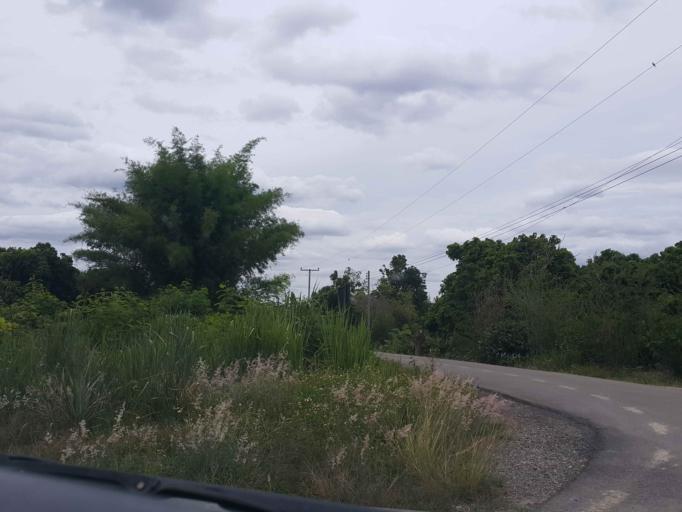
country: TH
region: Chiang Mai
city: Doi Lo
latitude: 18.5205
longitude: 98.7734
